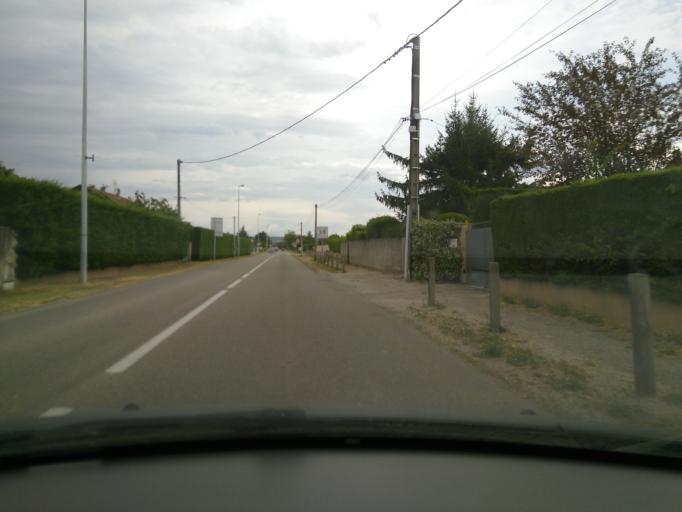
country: FR
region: Rhone-Alpes
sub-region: Departement de l'Isere
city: Beaurepaire
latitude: 45.3425
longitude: 5.0466
